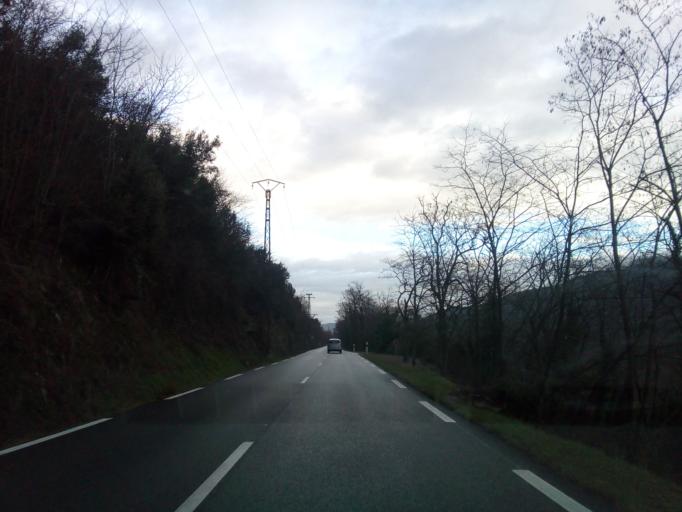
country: FR
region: Rhone-Alpes
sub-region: Departement de l'Ardeche
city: Saint-Sauveur-de-Montagut
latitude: 44.8208
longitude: 4.6438
